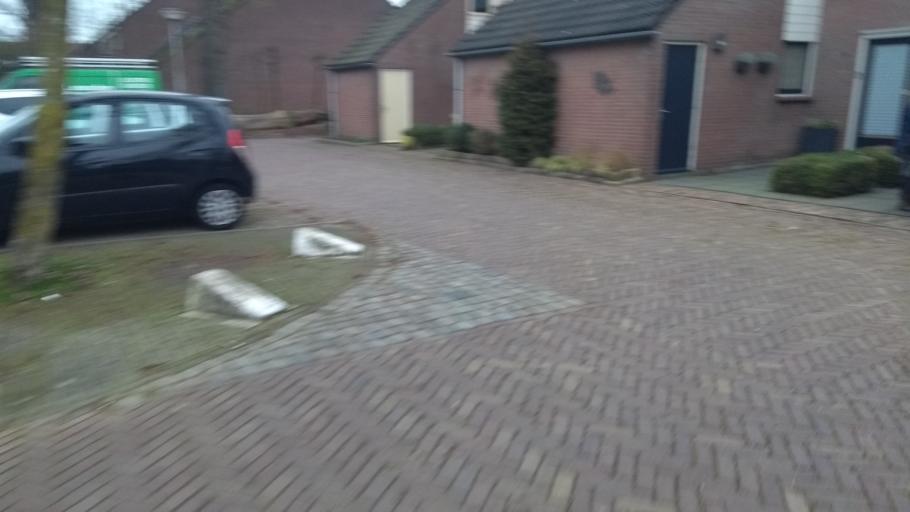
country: NL
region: Overijssel
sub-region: Gemeente Almelo
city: Almelo
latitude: 52.3774
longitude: 6.6866
